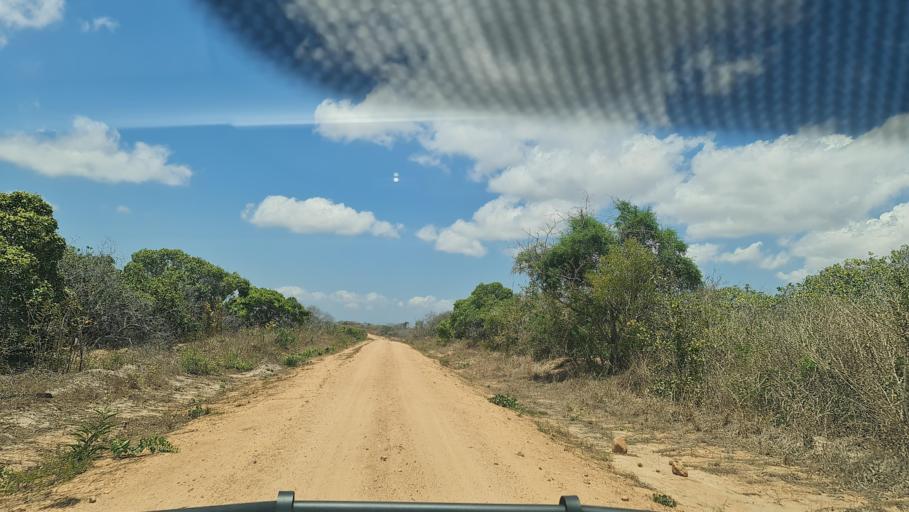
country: MZ
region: Nampula
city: Nacala
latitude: -14.3212
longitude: 40.5867
